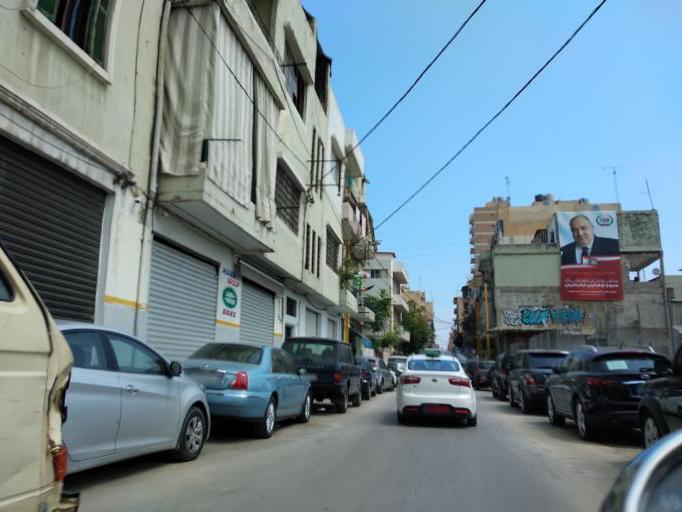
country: LB
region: Mont-Liban
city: Jdaidet el Matn
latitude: 33.8920
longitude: 35.5330
